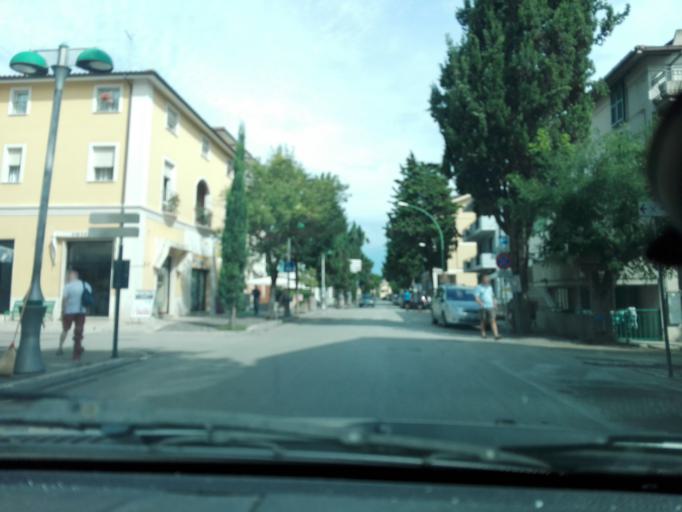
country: IT
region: Abruzzo
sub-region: Provincia di Teramo
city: Pineto
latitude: 42.6087
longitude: 14.0665
